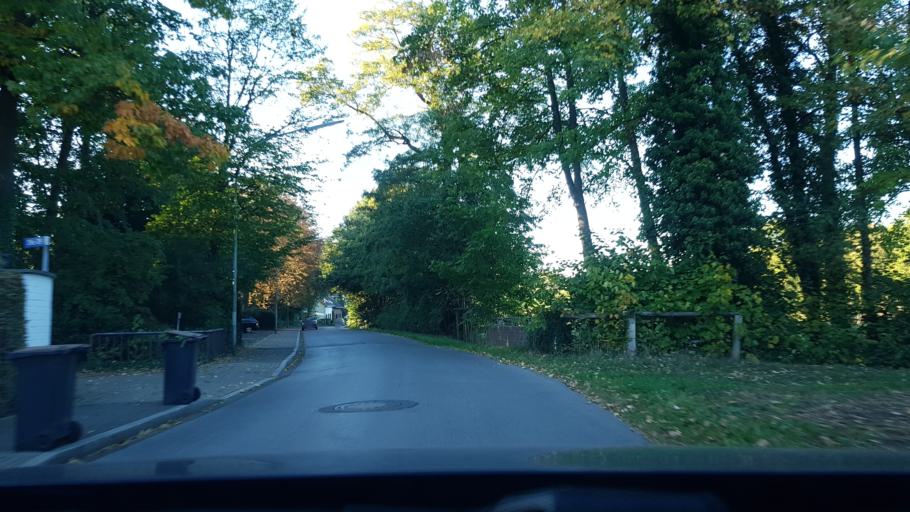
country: DE
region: North Rhine-Westphalia
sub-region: Regierungsbezirk Dusseldorf
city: Moers
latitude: 51.4396
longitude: 6.5802
